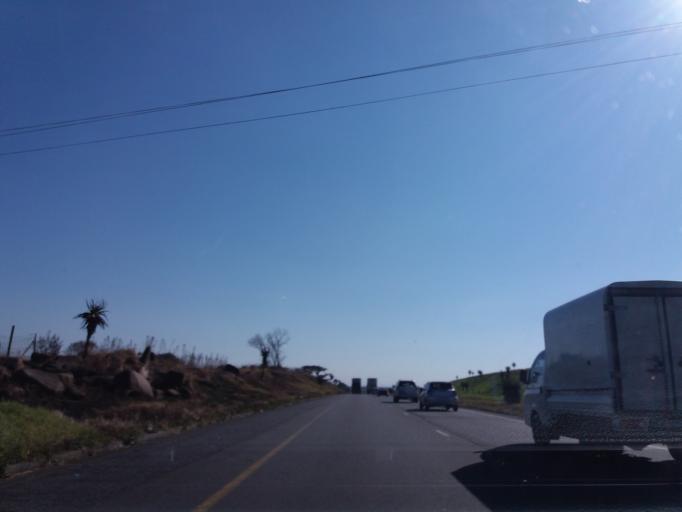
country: ZA
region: KwaZulu-Natal
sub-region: uMgungundlovu District Municipality
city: Camperdown
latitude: -29.7294
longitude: 30.5136
